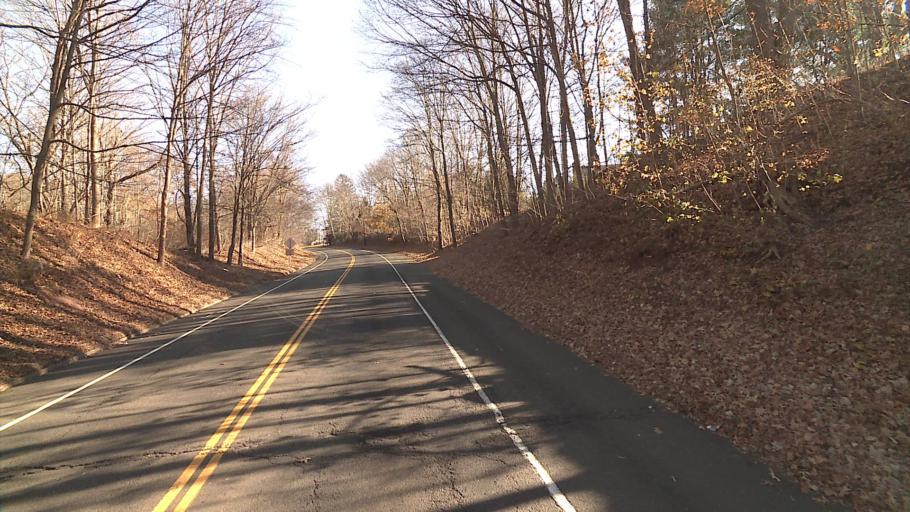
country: US
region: Connecticut
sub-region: New Haven County
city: North Haven
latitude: 41.3804
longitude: -72.8065
